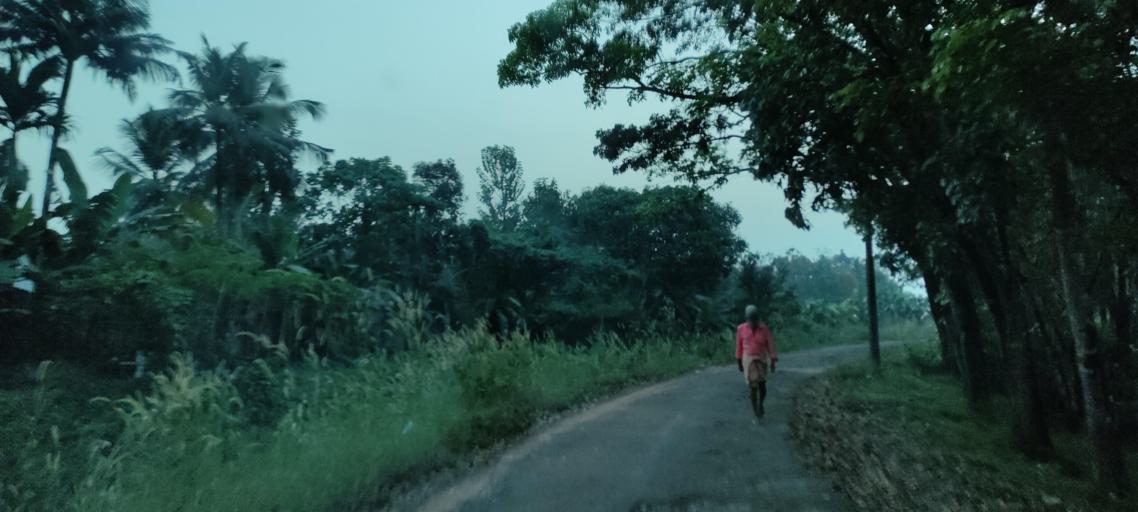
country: IN
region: Kerala
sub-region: Pattanamtitta
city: Adur
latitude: 9.1614
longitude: 76.7461
